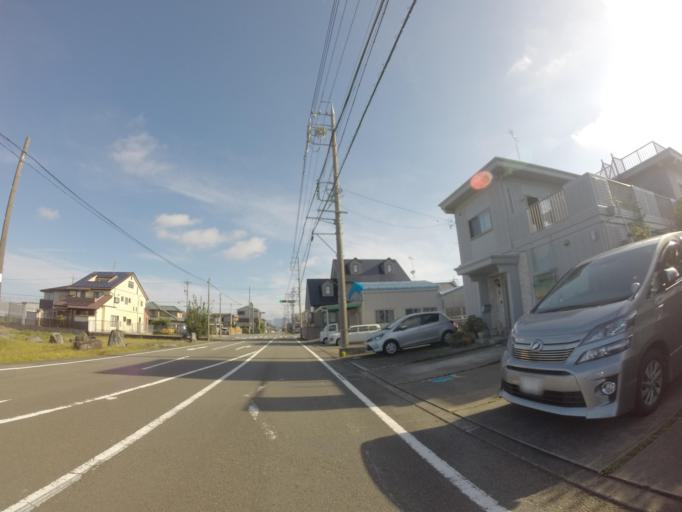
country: JP
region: Shizuoka
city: Yaizu
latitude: 34.8268
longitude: 138.3110
